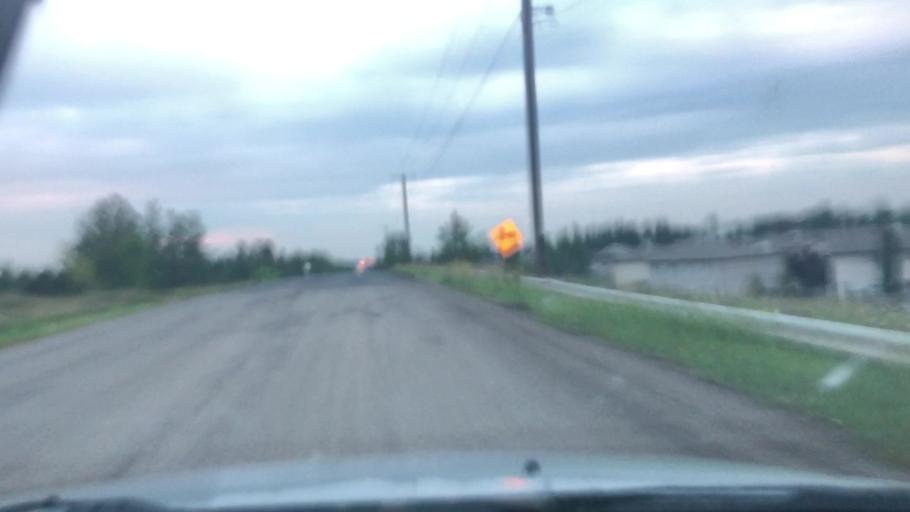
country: CA
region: Alberta
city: Devon
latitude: 53.4843
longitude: -113.6889
